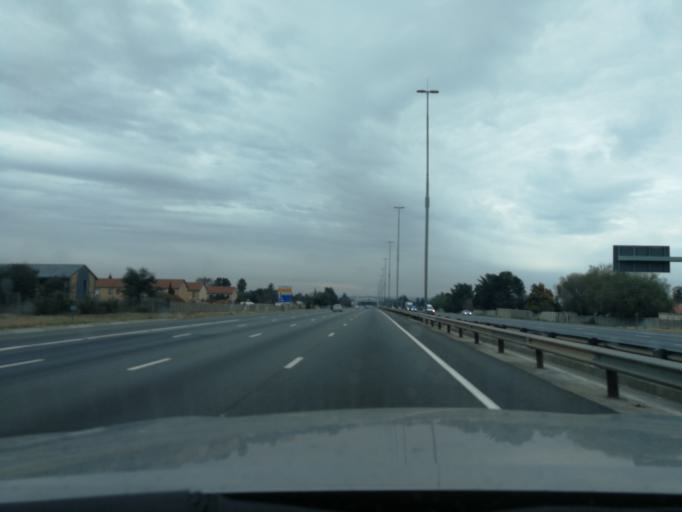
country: ZA
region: Gauteng
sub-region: Ekurhuleni Metropolitan Municipality
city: Germiston
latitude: -26.2686
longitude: 28.1500
